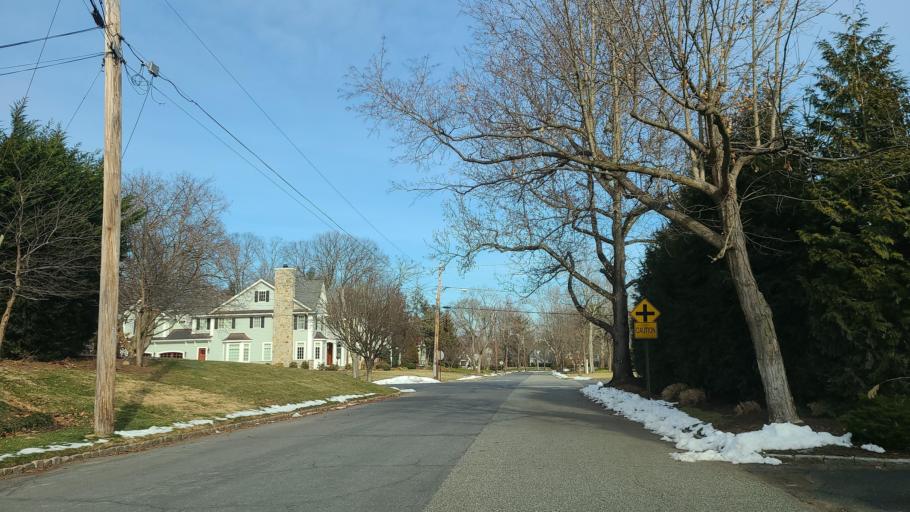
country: US
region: New Jersey
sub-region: Union County
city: Summit
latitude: 40.7338
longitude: -74.3484
